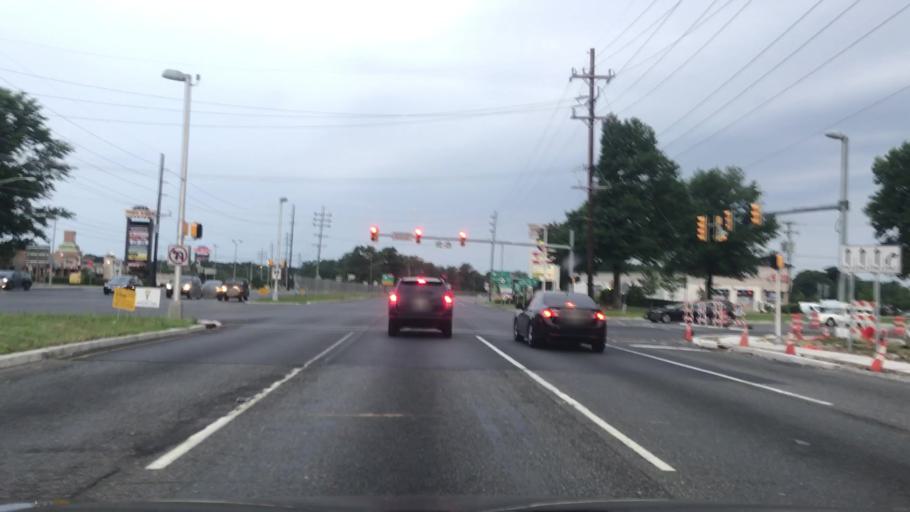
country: US
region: New Jersey
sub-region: Ocean County
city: Toms River
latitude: 39.9636
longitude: -74.2003
